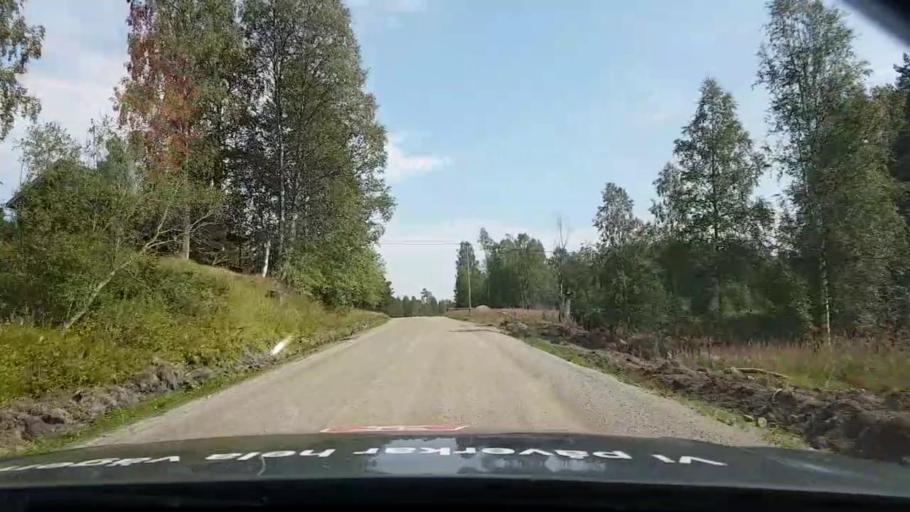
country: SE
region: Jaemtland
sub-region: Braecke Kommun
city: Braecke
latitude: 62.7249
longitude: 15.5349
